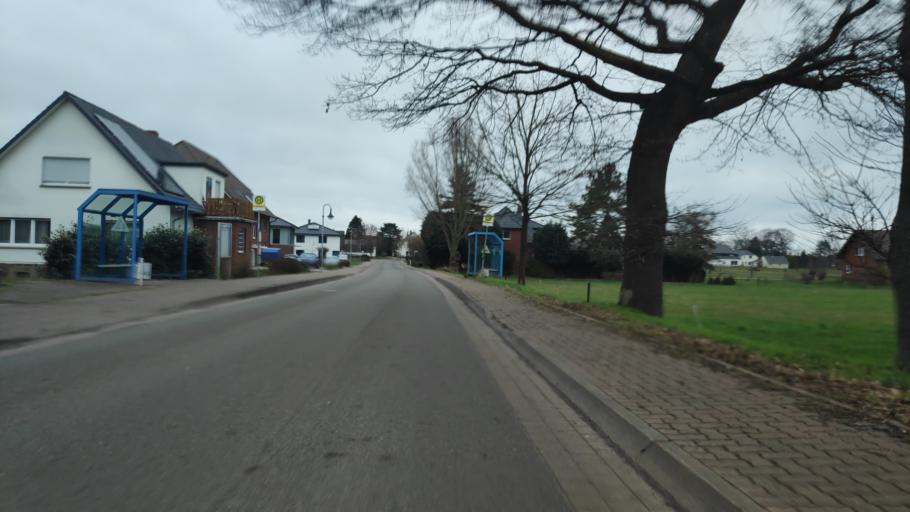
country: DE
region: North Rhine-Westphalia
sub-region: Regierungsbezirk Detmold
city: Hille
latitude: 52.3381
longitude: 8.8031
